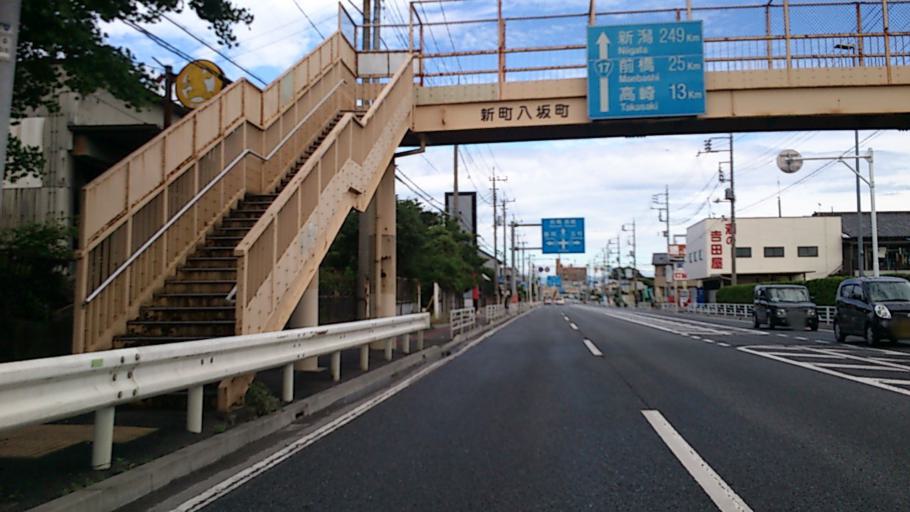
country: JP
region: Gunma
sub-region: Sawa-gun
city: Tamamura
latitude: 36.2711
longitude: 139.1117
